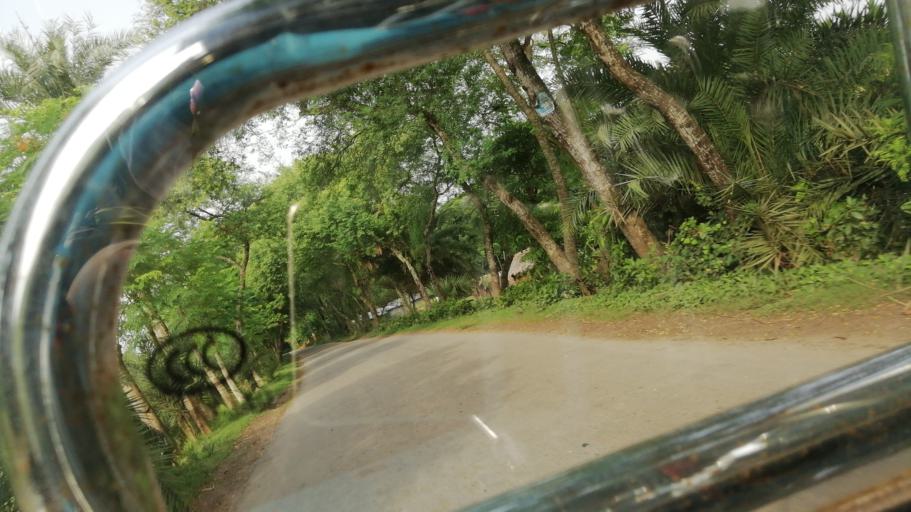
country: BD
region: Khulna
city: Kesabpur
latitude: 23.0291
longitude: 89.2683
